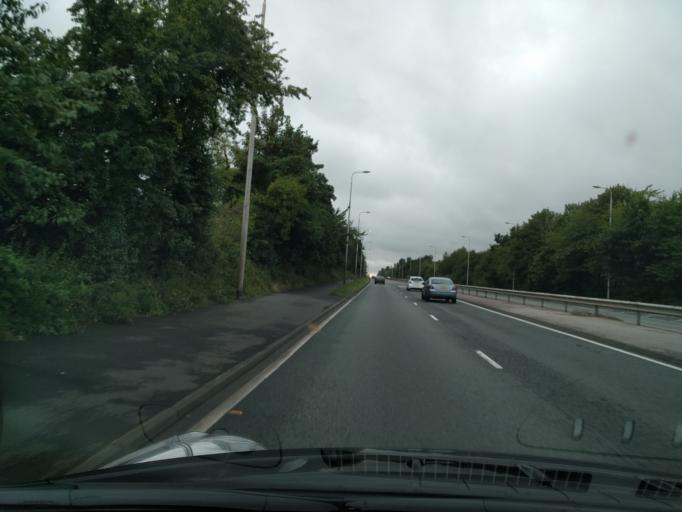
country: GB
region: England
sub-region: Borough of Wigan
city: Ashton in Makerfield
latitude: 53.4725
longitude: -2.6545
